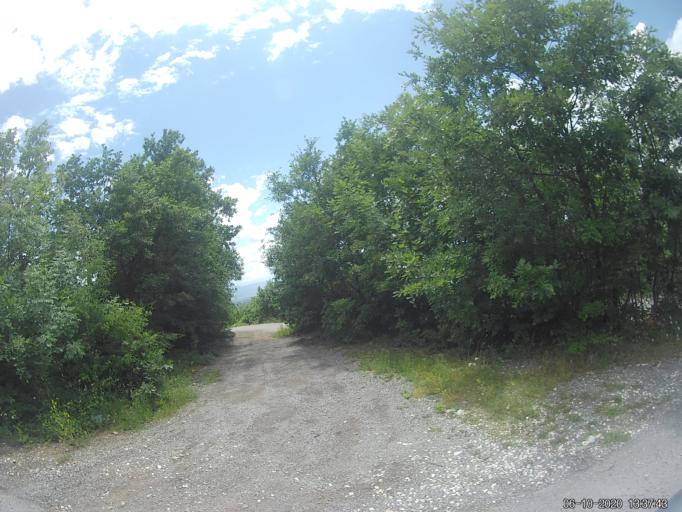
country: XK
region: Prizren
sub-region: Komuna e Therandes
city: Budakovo
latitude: 42.4086
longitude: 20.9015
